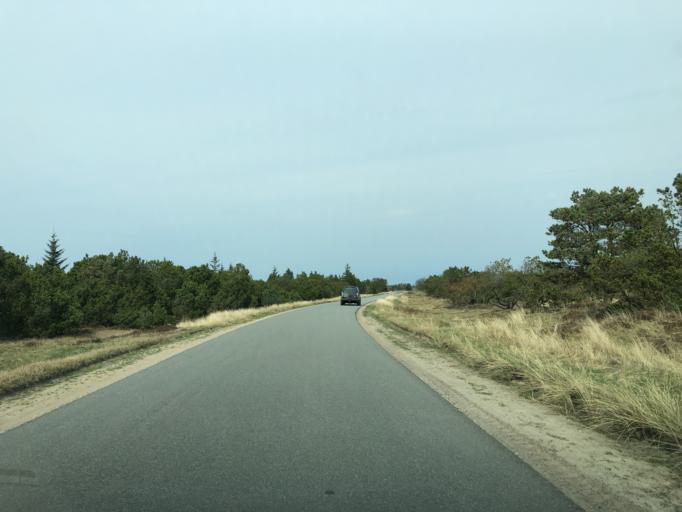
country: DK
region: South Denmark
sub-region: Varde Kommune
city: Oksbol
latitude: 55.6338
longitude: 8.1722
